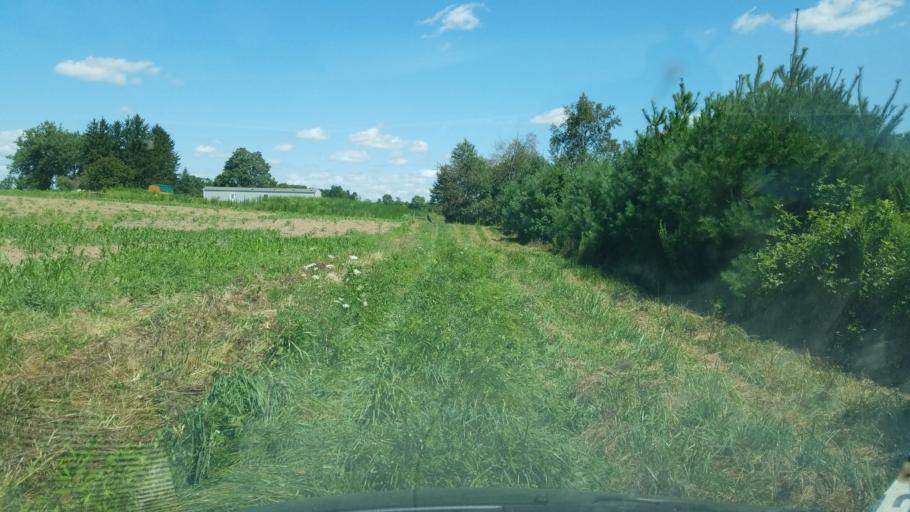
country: US
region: Ohio
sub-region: Morrow County
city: Mount Gilead
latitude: 40.5765
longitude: -82.8176
